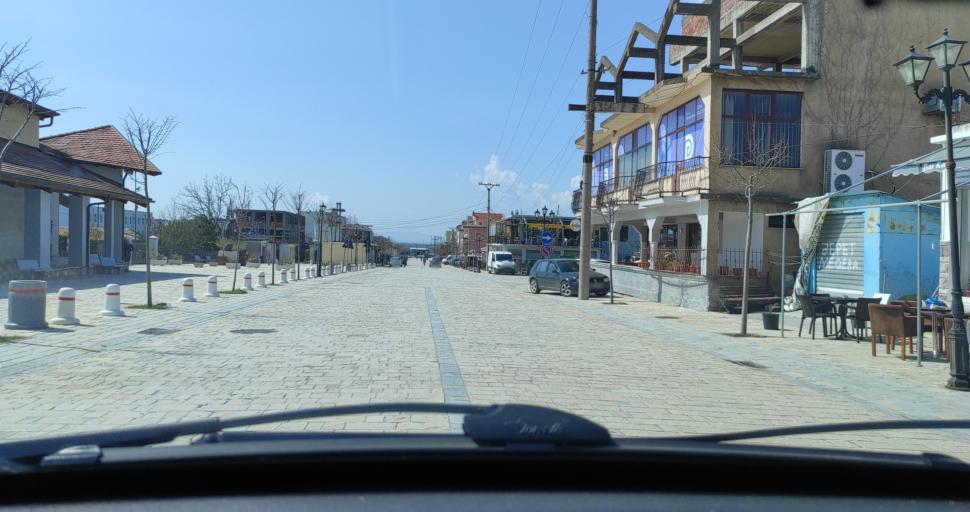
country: AL
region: Shkoder
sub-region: Rrethi i Shkodres
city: Vau i Dejes
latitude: 42.0077
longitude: 19.6409
